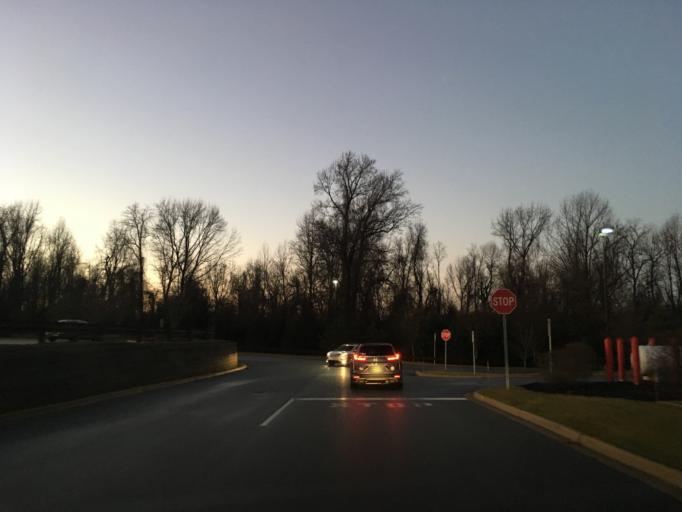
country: US
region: Pennsylvania
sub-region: Delaware County
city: Chester Heights
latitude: 39.8906
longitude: -75.5316
